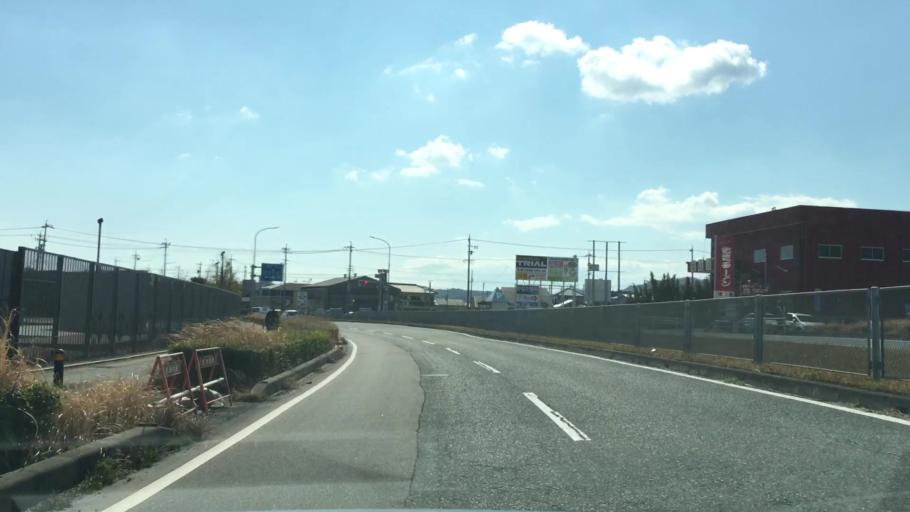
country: JP
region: Aichi
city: Gamagori
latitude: 34.8234
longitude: 137.2040
